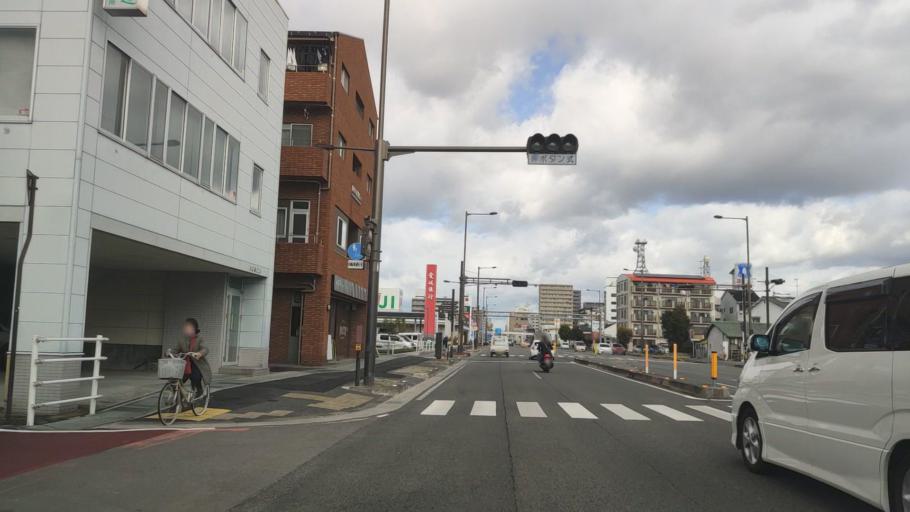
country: JP
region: Ehime
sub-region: Shikoku-chuo Shi
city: Matsuyama
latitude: 33.8290
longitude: 132.7588
